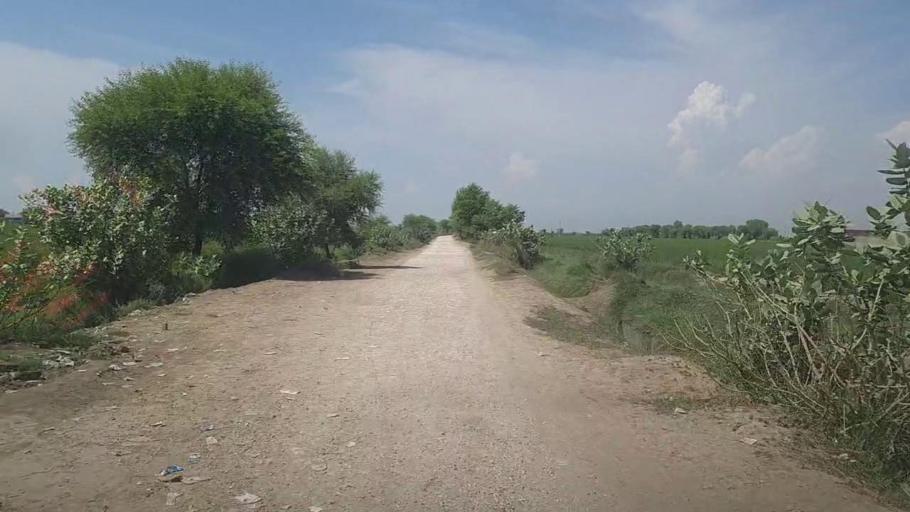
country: PK
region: Sindh
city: Kandhkot
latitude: 28.3026
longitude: 69.2444
